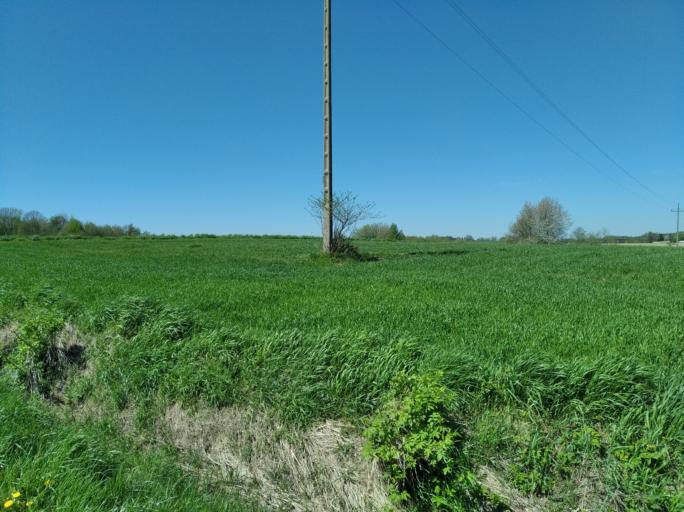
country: PL
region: Subcarpathian Voivodeship
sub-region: Powiat ropczycko-sedziszowski
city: Wielopole Skrzynskie
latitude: 49.9132
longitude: 21.5439
